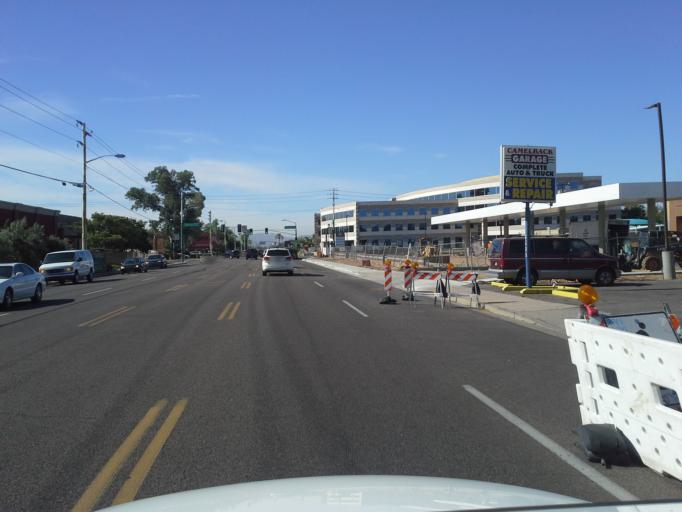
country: US
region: Arizona
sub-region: Maricopa County
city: Phoenix
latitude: 33.5177
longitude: -112.0651
